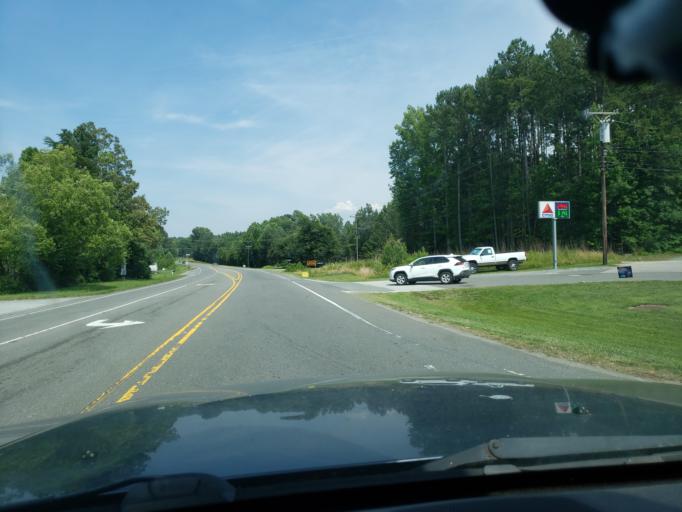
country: US
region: North Carolina
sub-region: Orange County
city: Carrboro
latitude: 35.9220
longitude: -79.1872
